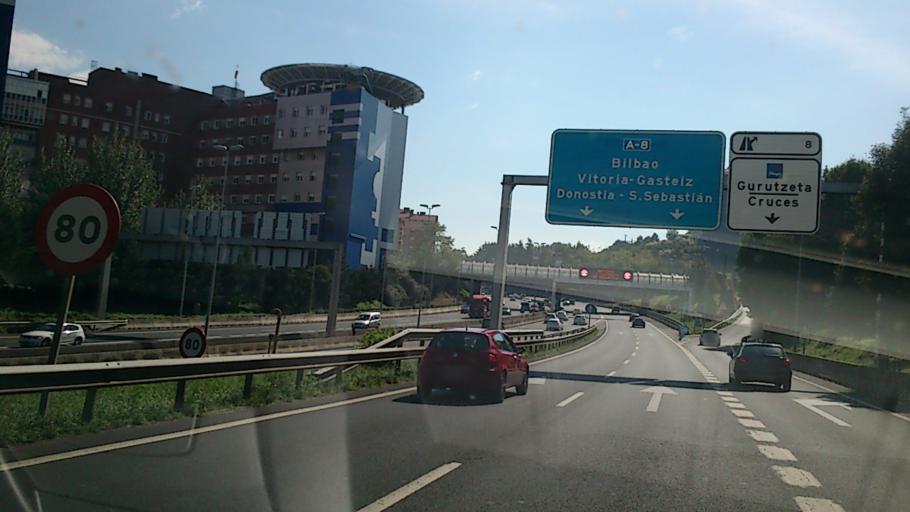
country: ES
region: Basque Country
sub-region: Bizkaia
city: Barakaldo
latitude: 43.2827
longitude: -2.9867
